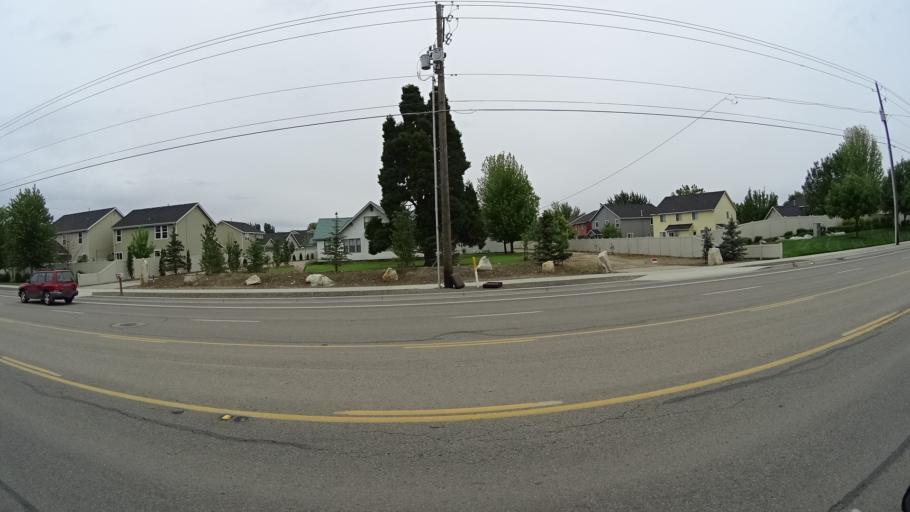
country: US
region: Idaho
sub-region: Ada County
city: Meridian
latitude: 43.6340
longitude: -116.3406
